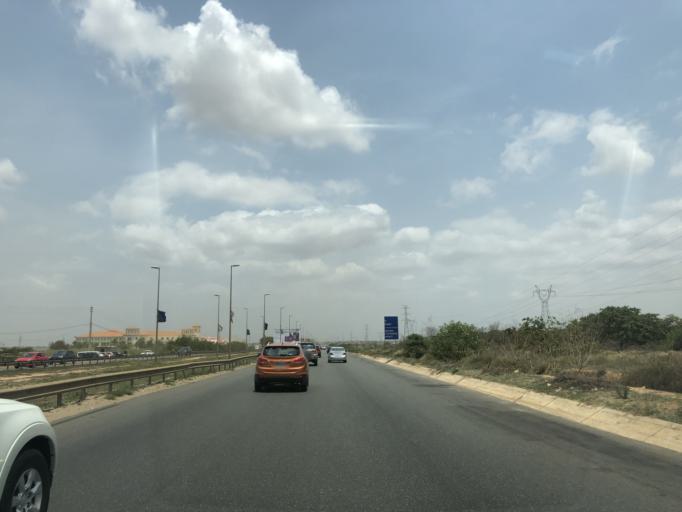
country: AO
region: Luanda
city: Luanda
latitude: -8.9734
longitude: 13.2670
